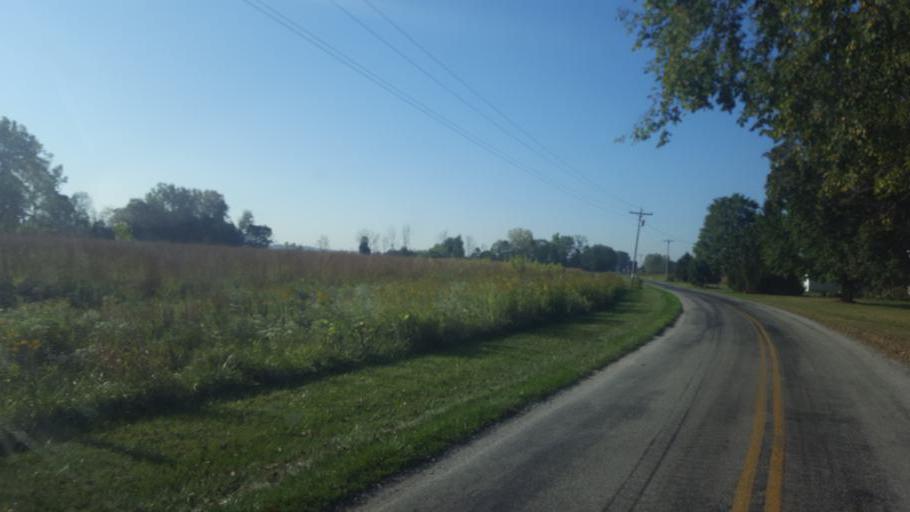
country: US
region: Ohio
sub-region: Union County
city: Richwood
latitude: 40.5567
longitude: -83.3315
